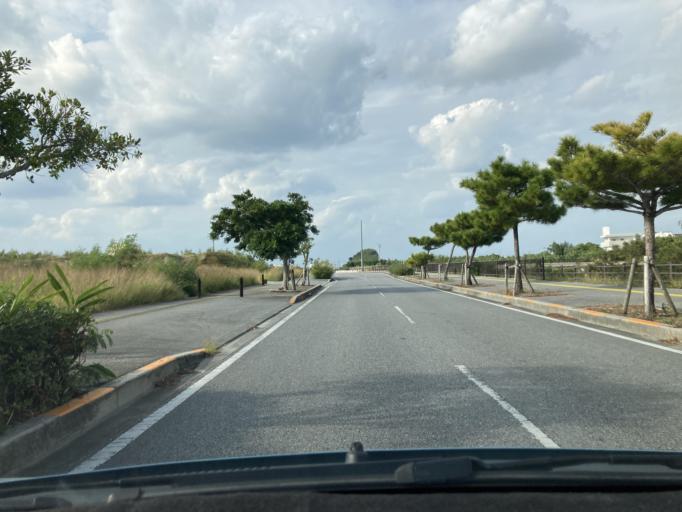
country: JP
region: Okinawa
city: Itoman
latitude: 26.1565
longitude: 127.6659
